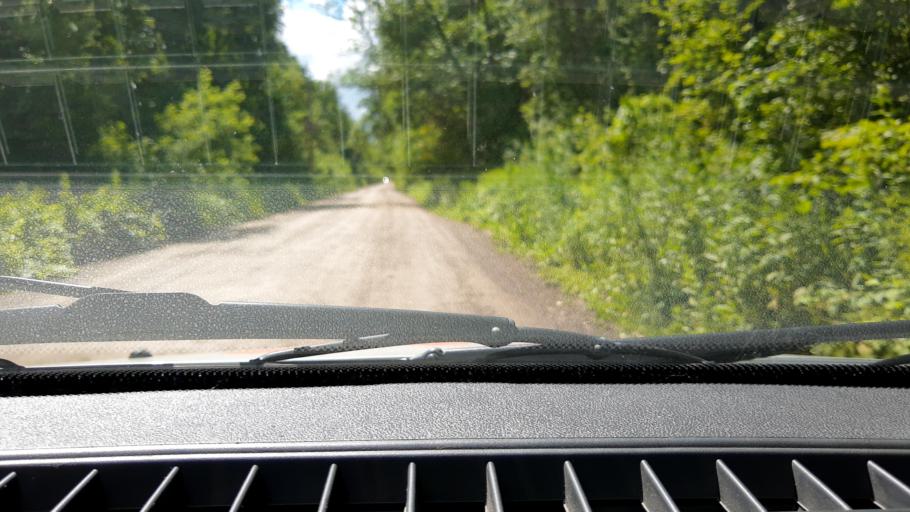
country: RU
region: Bashkortostan
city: Ufa
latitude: 54.6908
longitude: 56.0532
